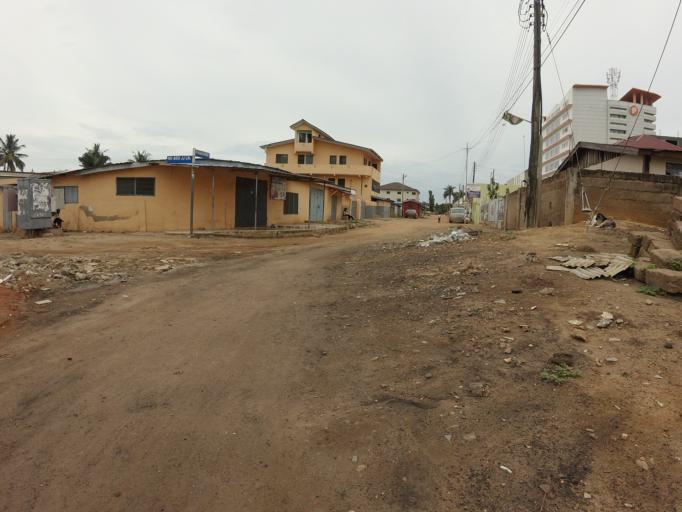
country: GH
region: Greater Accra
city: Accra
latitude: 5.5999
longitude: -0.2233
